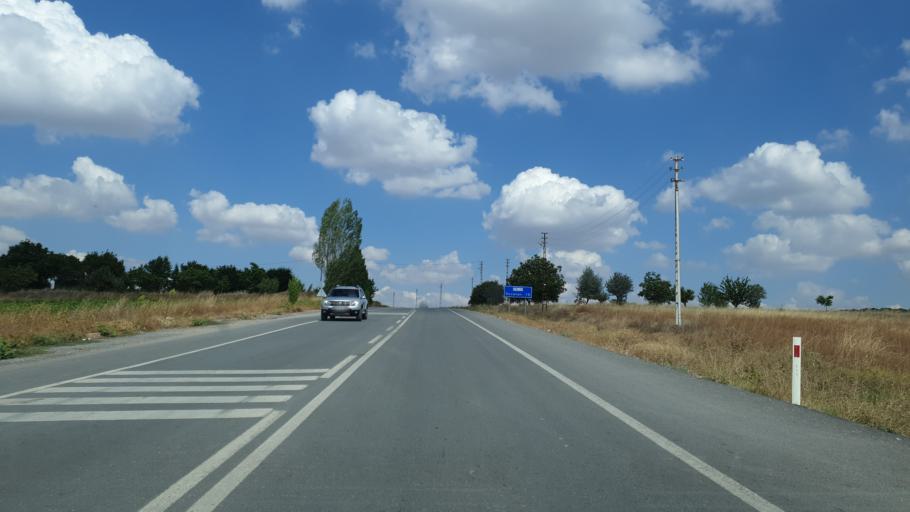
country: TR
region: Kayseri
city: Felahiye
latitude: 39.0955
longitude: 35.5782
